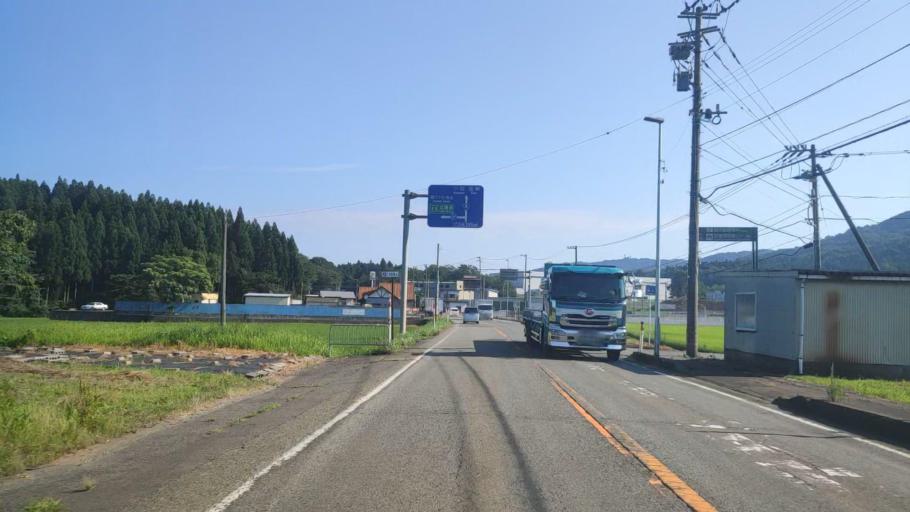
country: JP
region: Fukui
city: Maruoka
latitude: 36.2345
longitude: 136.2868
